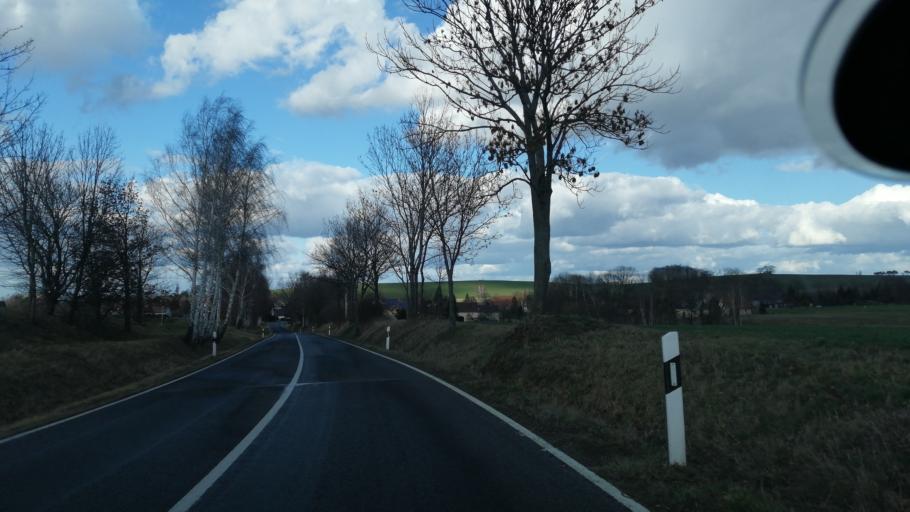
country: DE
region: Saxony
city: Cunewalde
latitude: 51.1391
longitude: 14.5346
